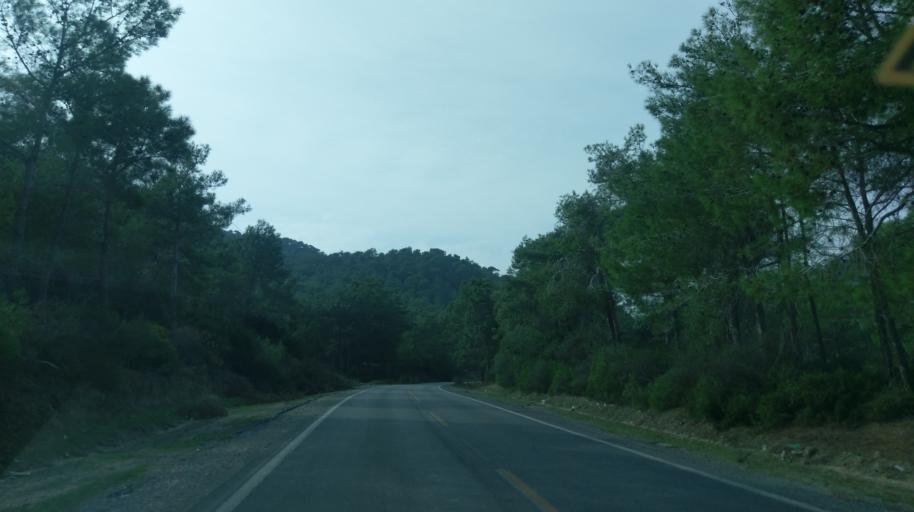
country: CY
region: Keryneia
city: Lapithos
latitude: 35.3450
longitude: 33.0803
